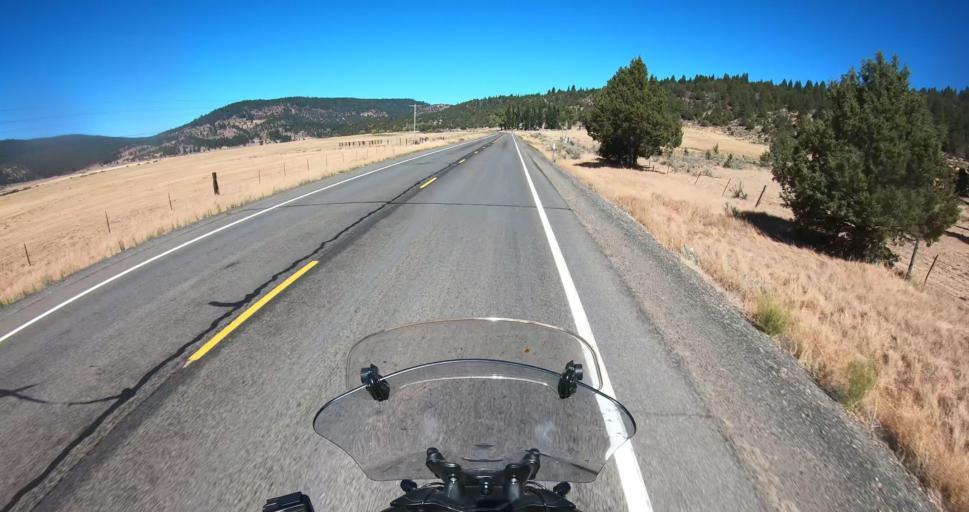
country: US
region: Oregon
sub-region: Lake County
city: Lakeview
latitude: 42.3675
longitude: -120.2968
